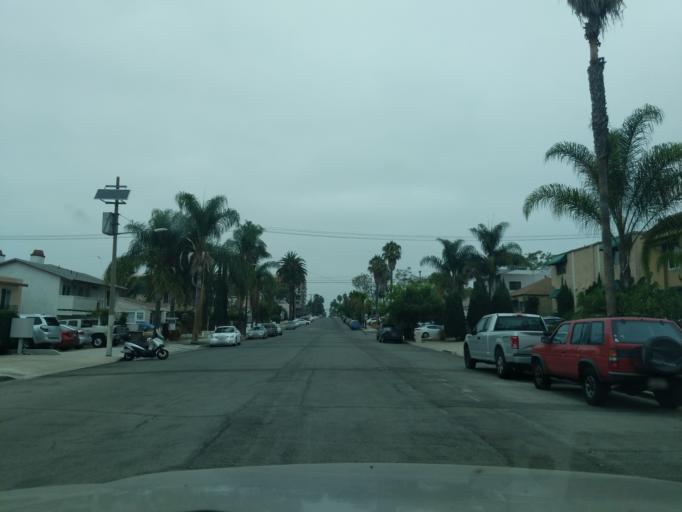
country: US
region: California
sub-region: San Diego County
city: San Diego
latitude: 32.7532
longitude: -117.1425
